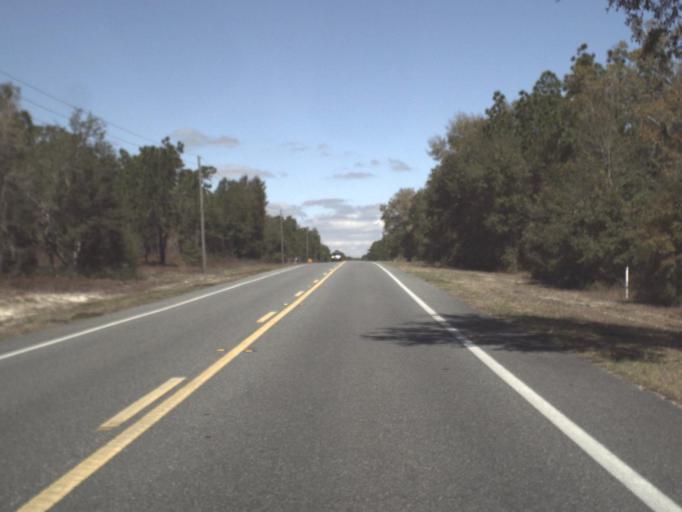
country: US
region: Florida
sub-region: Wakulla County
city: Crawfordville
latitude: 30.0642
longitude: -84.3887
